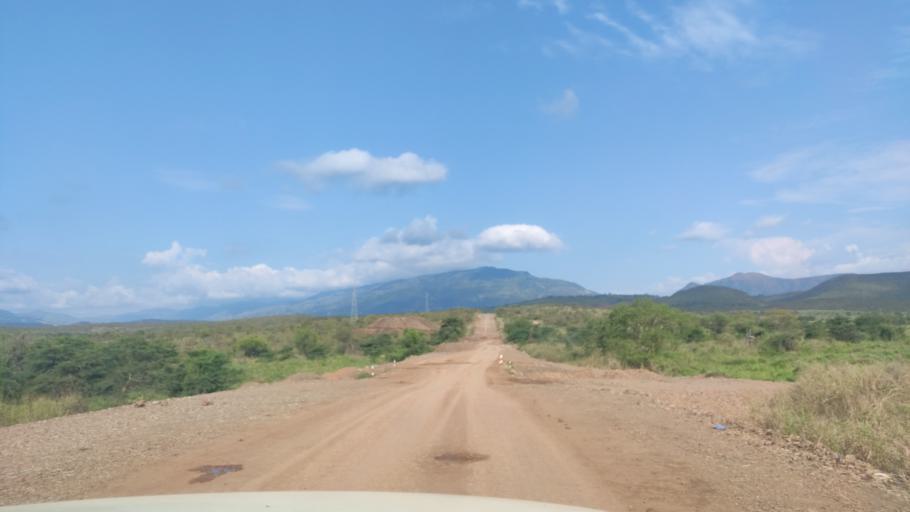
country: ET
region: Southern Nations, Nationalities, and People's Region
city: Felege Neway
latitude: 6.4342
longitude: 37.2681
